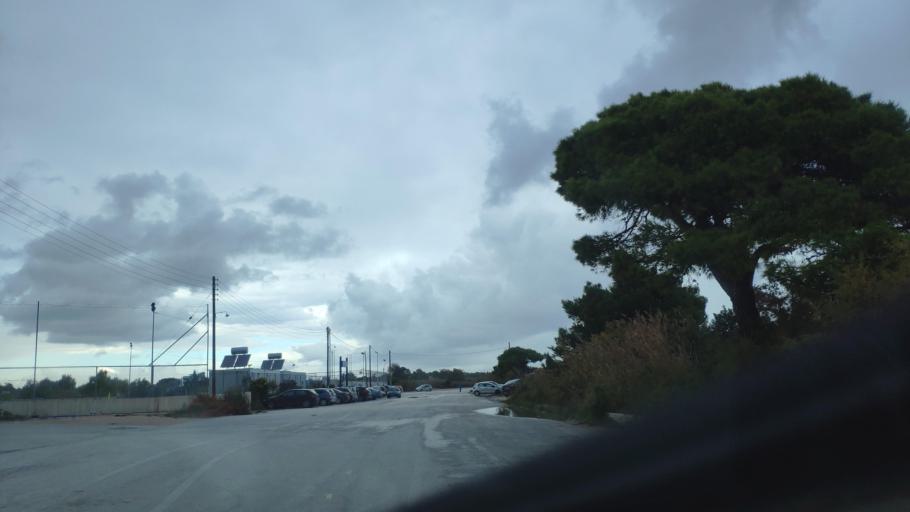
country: GR
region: Attica
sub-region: Nomarchia Anatolikis Attikis
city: Artemida
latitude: 37.9862
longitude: 24.0136
